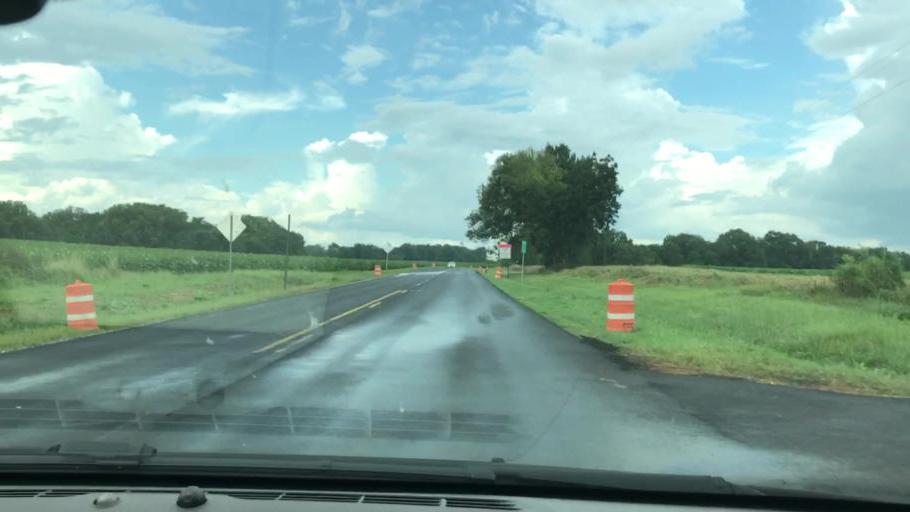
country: US
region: Georgia
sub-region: Early County
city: Blakely
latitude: 31.4291
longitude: -84.9700
